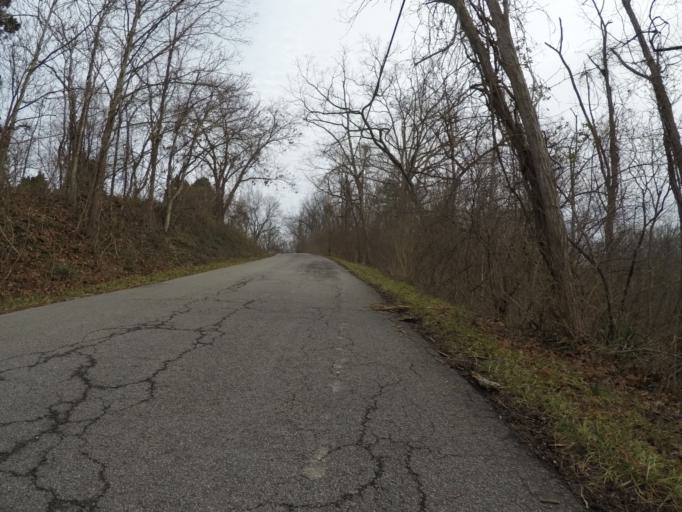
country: US
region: West Virginia
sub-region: Wayne County
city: Lavalette
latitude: 38.3644
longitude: -82.4192
